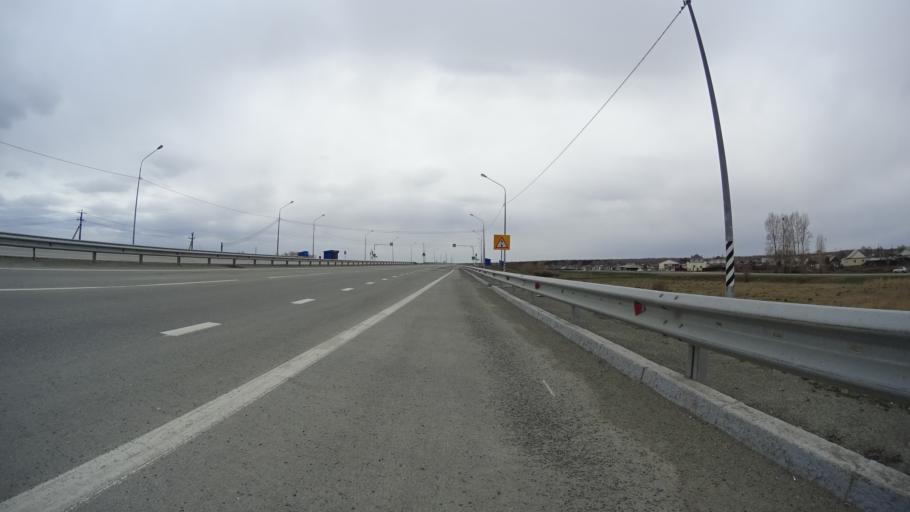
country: RU
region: Chelyabinsk
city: Yemanzhelinka
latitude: 54.7975
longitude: 61.3076
